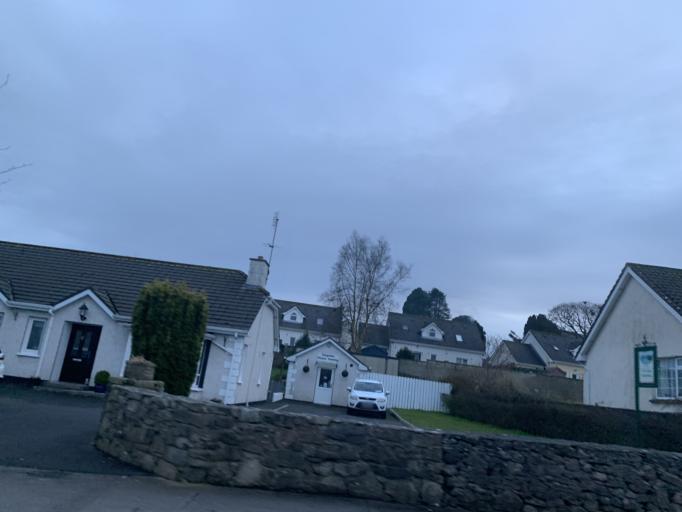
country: IE
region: Connaught
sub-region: Sligo
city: Collooney
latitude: 54.1835
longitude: -8.4901
